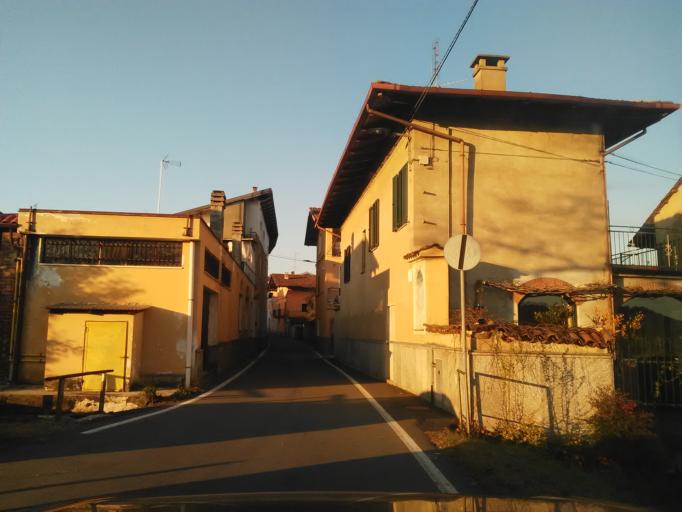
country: IT
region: Piedmont
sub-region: Provincia di Biella
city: Cerrione
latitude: 45.4671
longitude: 8.0696
